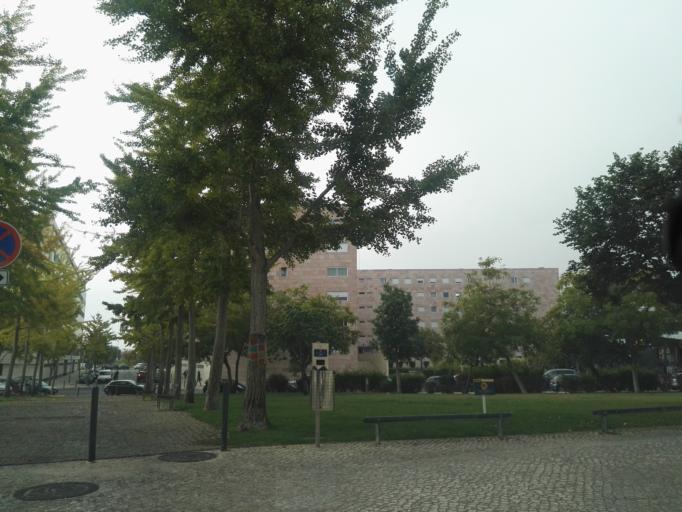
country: PT
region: Lisbon
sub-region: Loures
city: Moscavide
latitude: 38.7559
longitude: -9.0954
